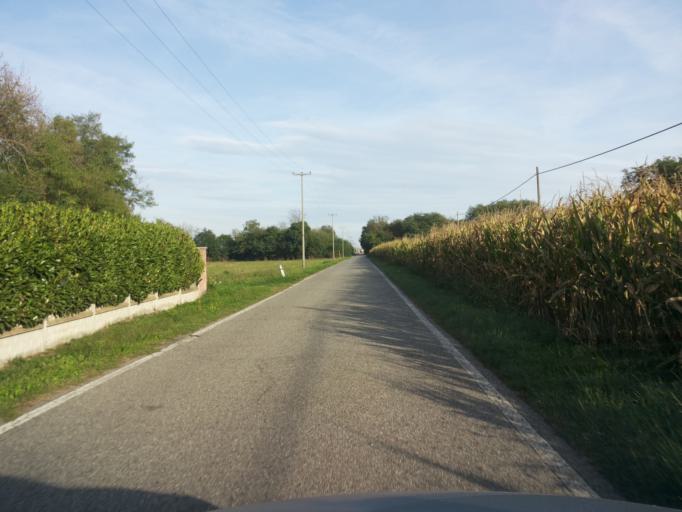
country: IT
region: Piedmont
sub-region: Provincia di Biella
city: Salussola
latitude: 45.4486
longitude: 8.1247
